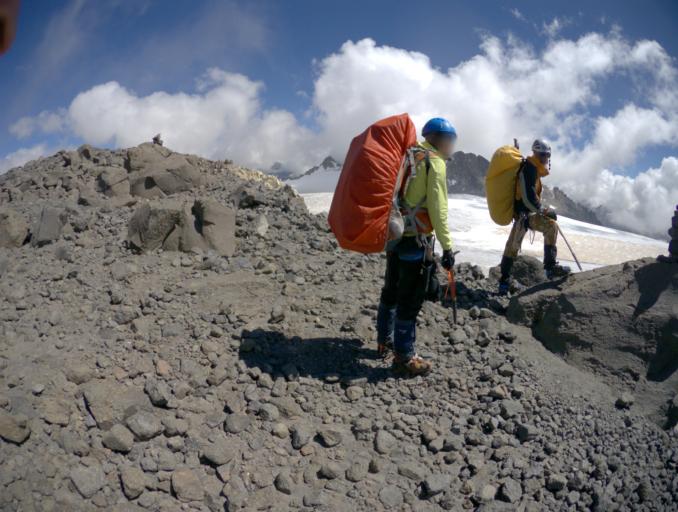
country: RU
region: Kabardino-Balkariya
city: Terskol
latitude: 43.3438
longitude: 42.5085
